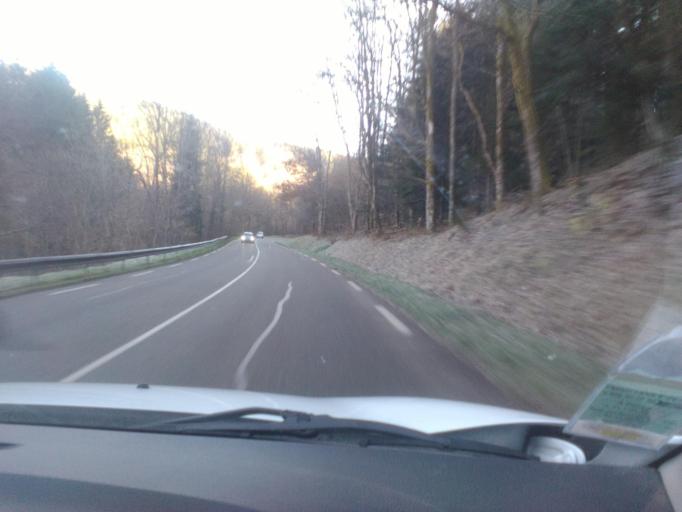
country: FR
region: Alsace
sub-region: Departement du Bas-Rhin
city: Rothau
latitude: 48.4150
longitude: 7.1732
